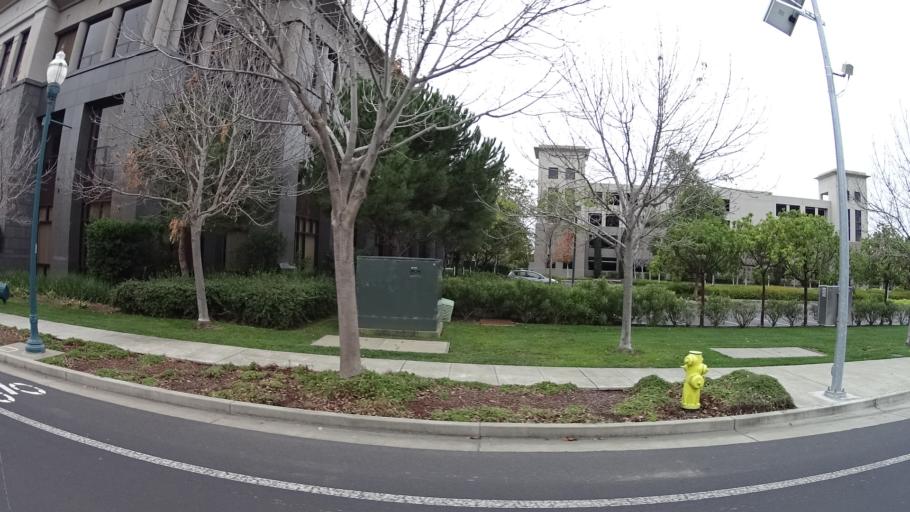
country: US
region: California
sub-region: San Mateo County
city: Foster City
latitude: 37.5451
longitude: -122.2938
